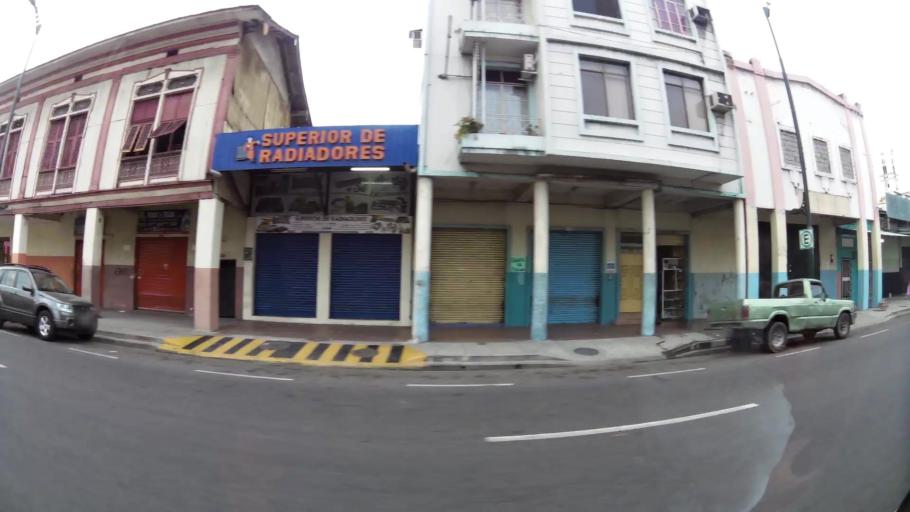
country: EC
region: Guayas
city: Guayaquil
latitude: -2.1922
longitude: -79.8908
